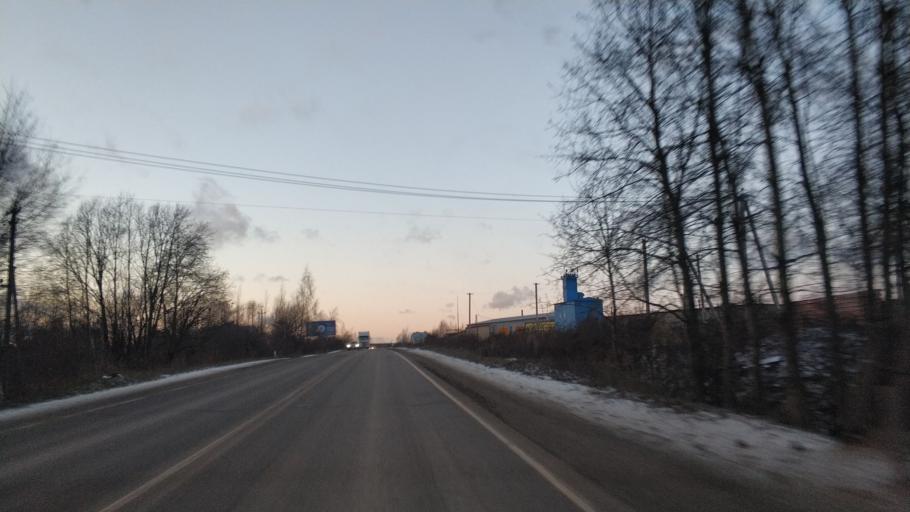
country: RU
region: St.-Petersburg
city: Pontonnyy
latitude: 59.8096
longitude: 30.6130
